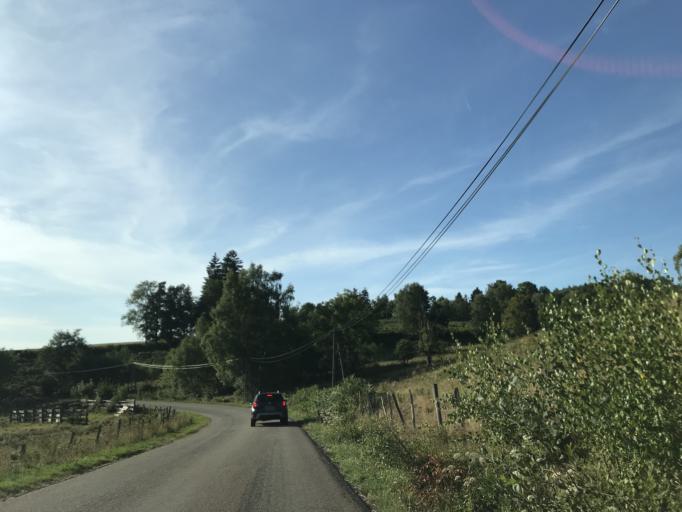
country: FR
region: Auvergne
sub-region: Departement du Puy-de-Dome
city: Job
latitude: 45.7010
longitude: 3.7260
